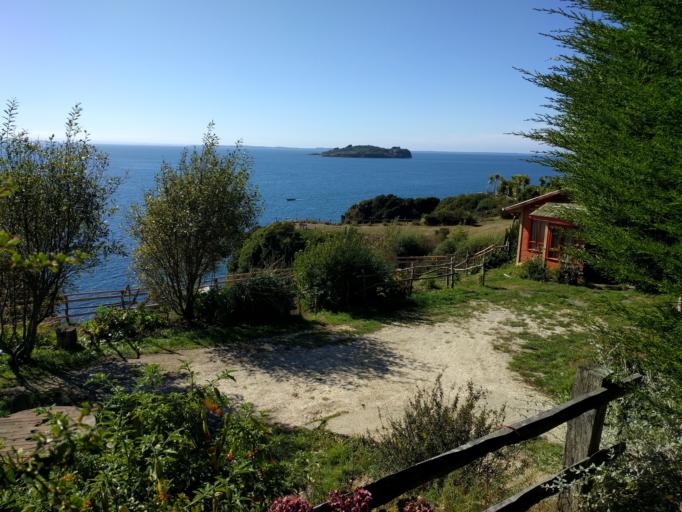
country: CL
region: Los Lagos
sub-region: Provincia de Chiloe
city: Ancud
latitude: -41.8604
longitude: -73.8232
